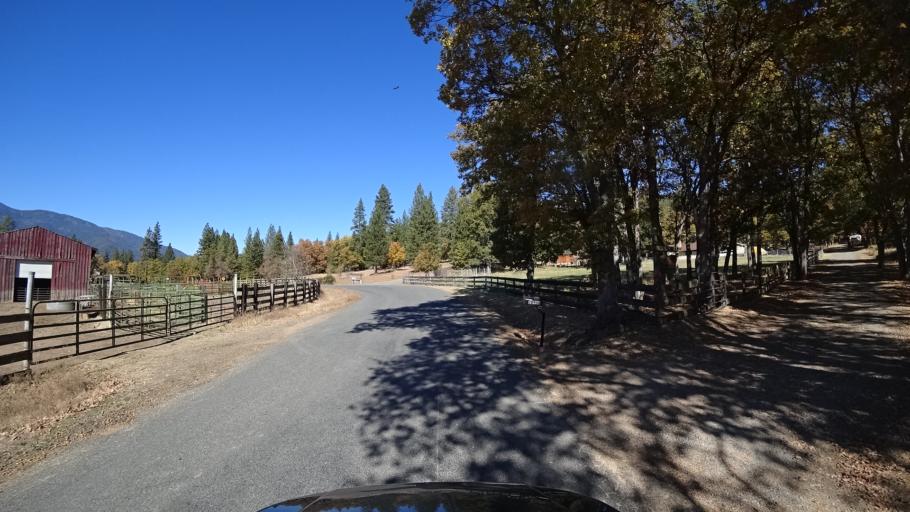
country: US
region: California
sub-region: Siskiyou County
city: Yreka
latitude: 41.5755
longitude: -122.9535
